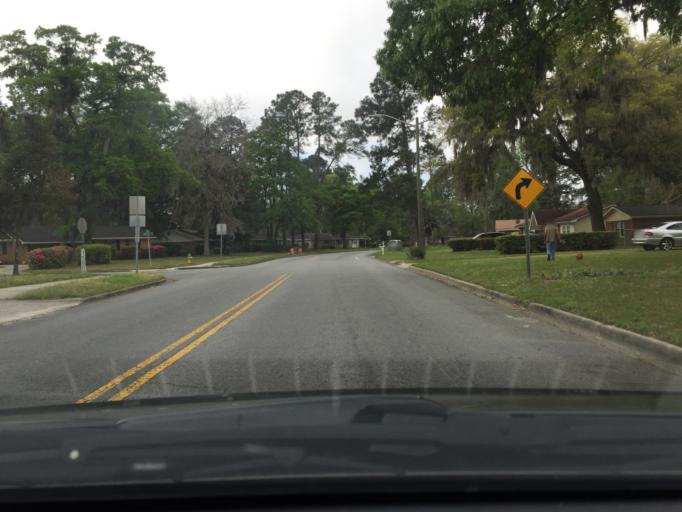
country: US
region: Georgia
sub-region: Chatham County
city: Montgomery
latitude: 31.9876
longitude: -81.1455
